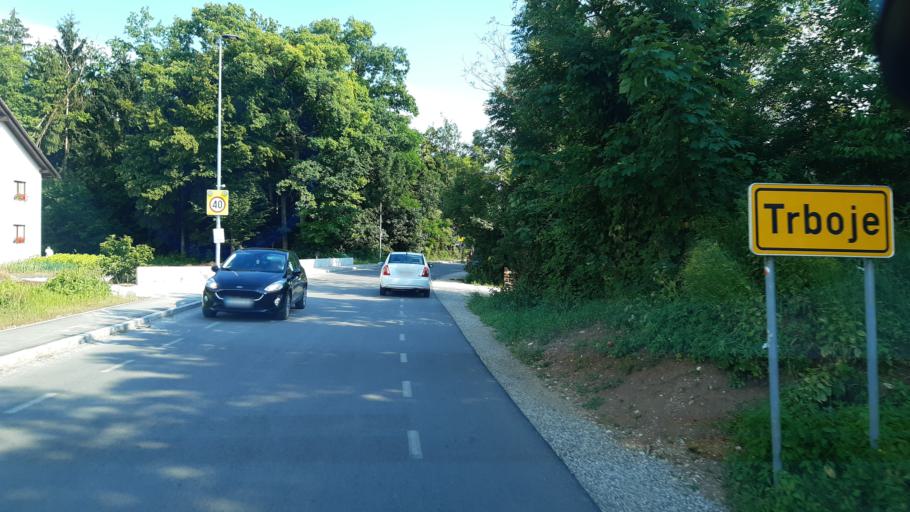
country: SI
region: Sencur
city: Hrastje
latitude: 46.2009
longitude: 14.4076
